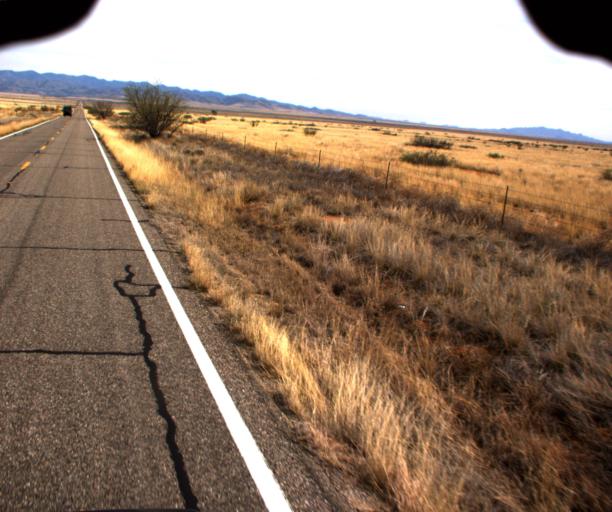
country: US
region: Arizona
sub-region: Cochise County
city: Willcox
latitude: 32.0868
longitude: -109.5276
